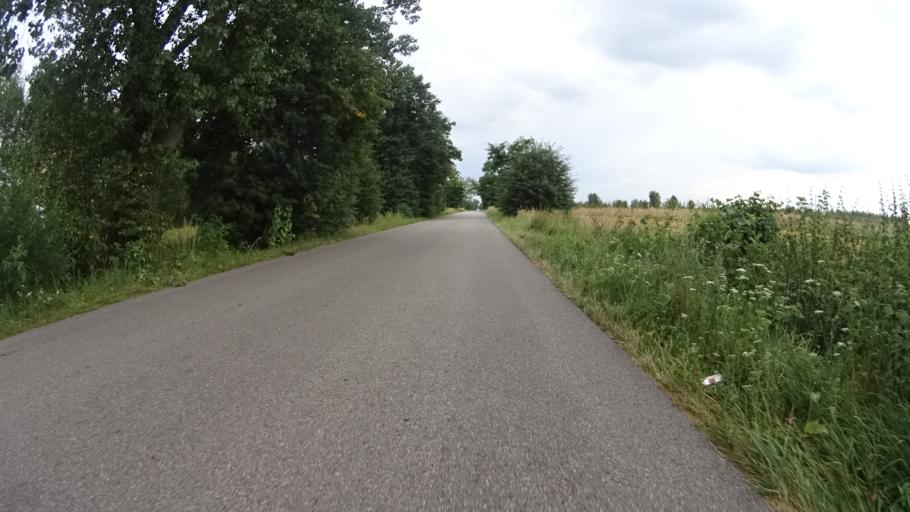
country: PL
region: Masovian Voivodeship
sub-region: Powiat grojecki
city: Goszczyn
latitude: 51.6764
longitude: 20.8589
